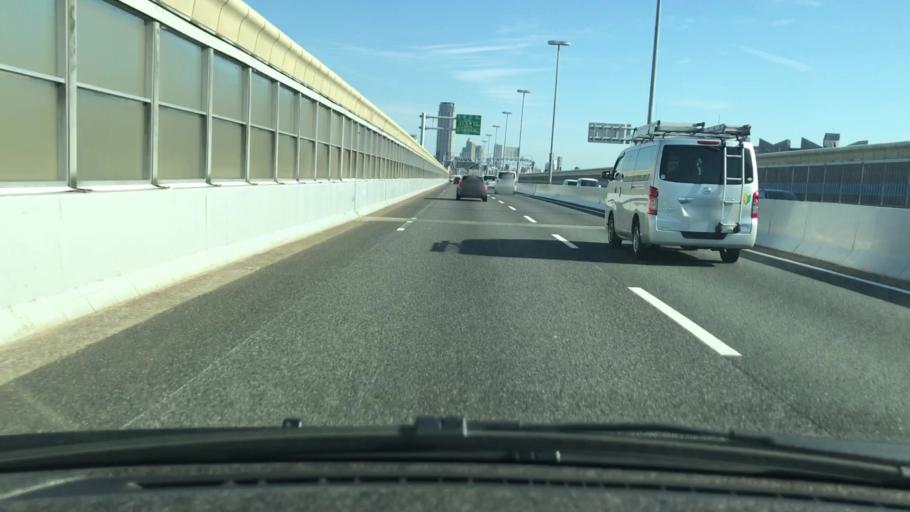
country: JP
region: Hyogo
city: Kobe
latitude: 34.7067
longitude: 135.2351
